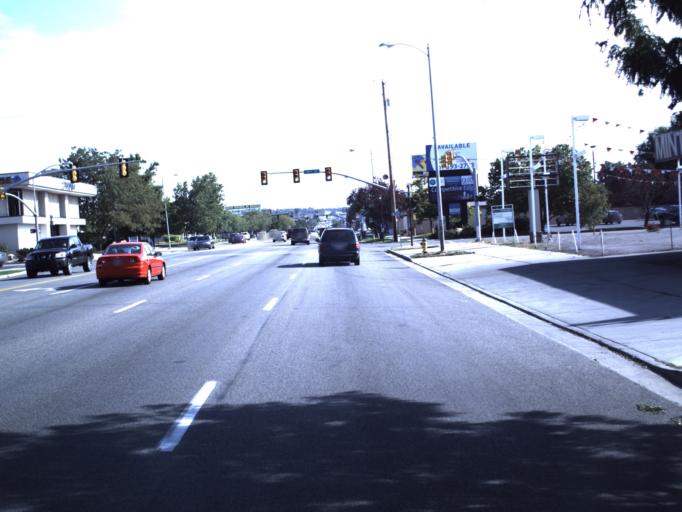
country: US
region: Utah
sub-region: Weber County
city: Ogden
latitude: 41.2130
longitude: -111.9708
